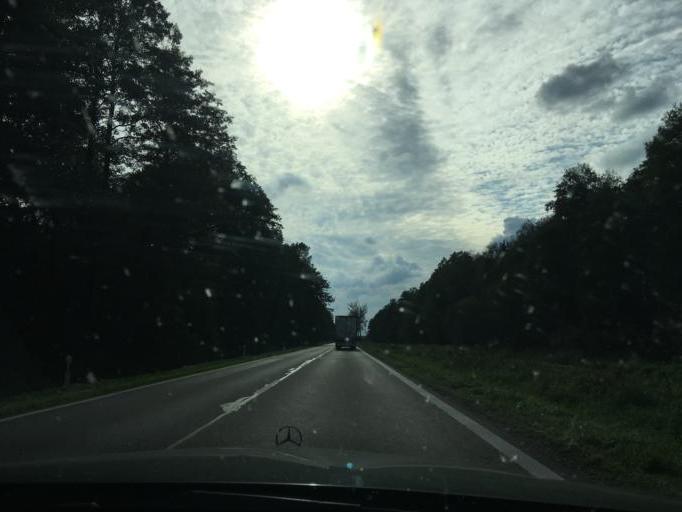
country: PL
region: Podlasie
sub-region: Powiat grajewski
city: Rajgrod
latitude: 53.6907
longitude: 22.6341
